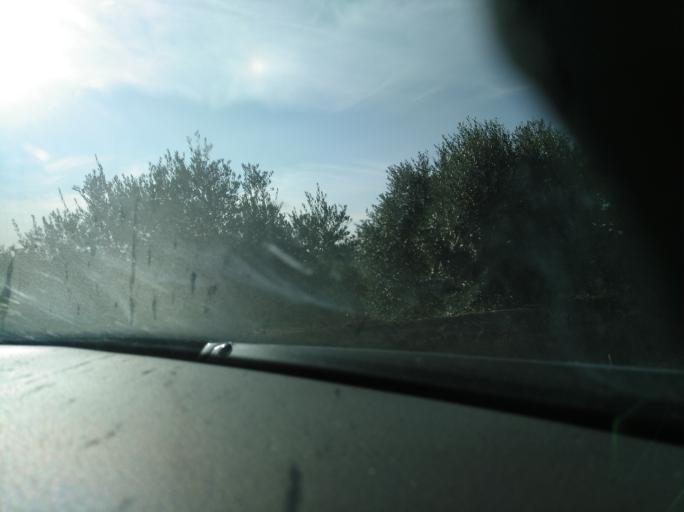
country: PT
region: Portalegre
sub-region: Elvas
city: Elvas
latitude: 38.8668
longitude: -7.2773
